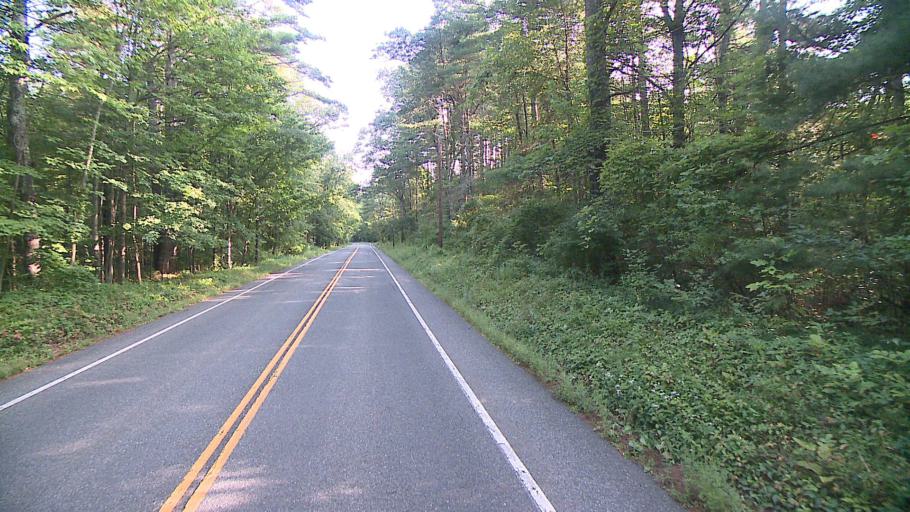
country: US
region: Connecticut
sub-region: Litchfield County
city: Kent
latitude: 41.8392
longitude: -73.3798
